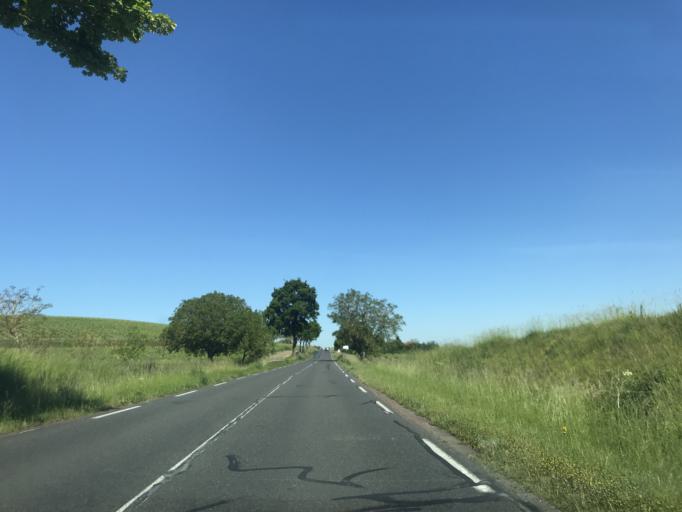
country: FR
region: Poitou-Charentes
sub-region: Departement de la Charente
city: Segonzac
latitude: 45.5199
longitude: -0.2902
